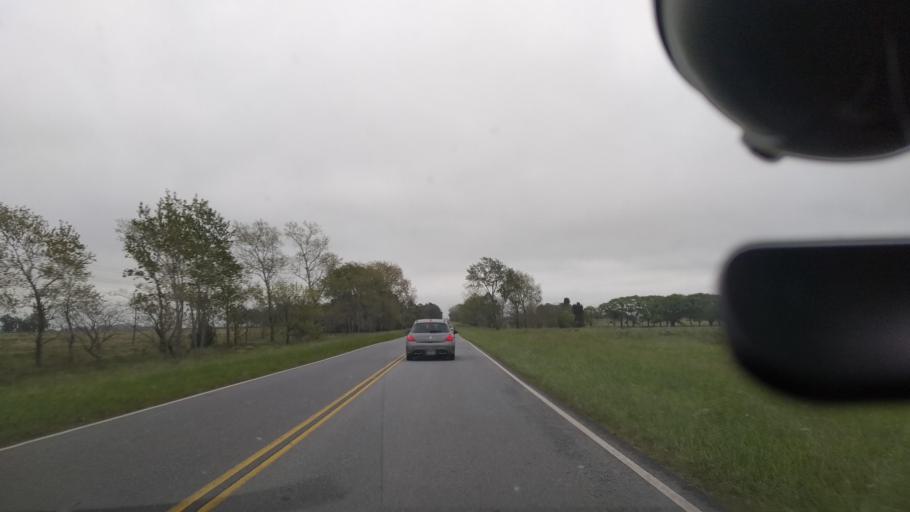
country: AR
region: Buenos Aires
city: Veronica
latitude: -35.3535
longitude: -57.4150
